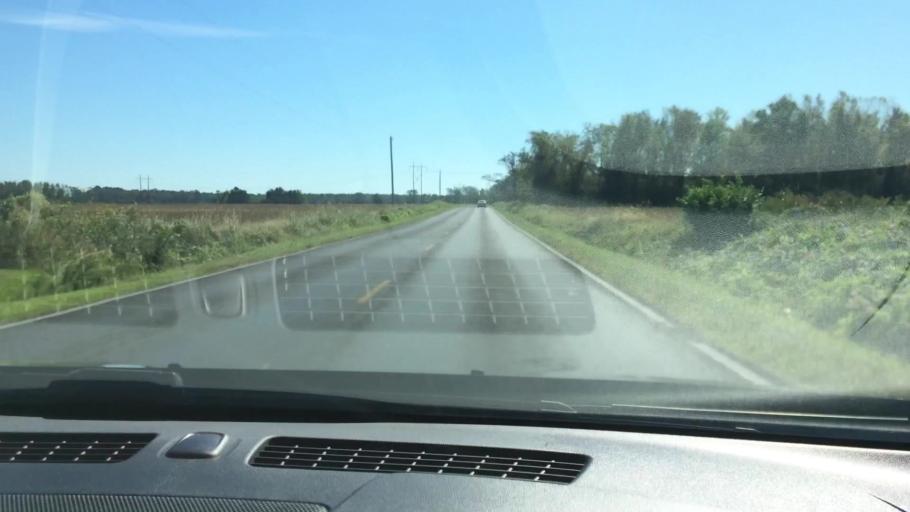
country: US
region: North Carolina
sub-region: Pitt County
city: Grifton
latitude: 35.3727
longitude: -77.3573
